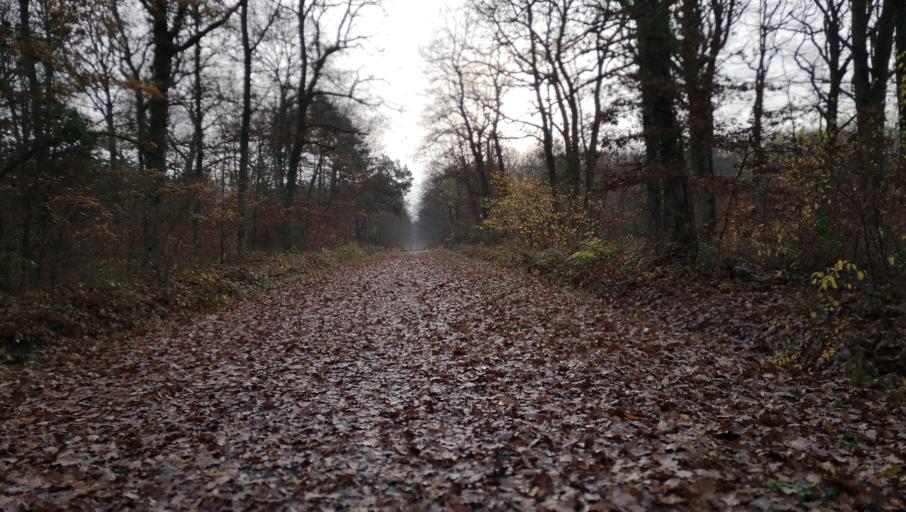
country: FR
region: Centre
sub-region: Departement du Loiret
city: Chanteau
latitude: 47.9453
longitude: 1.9687
